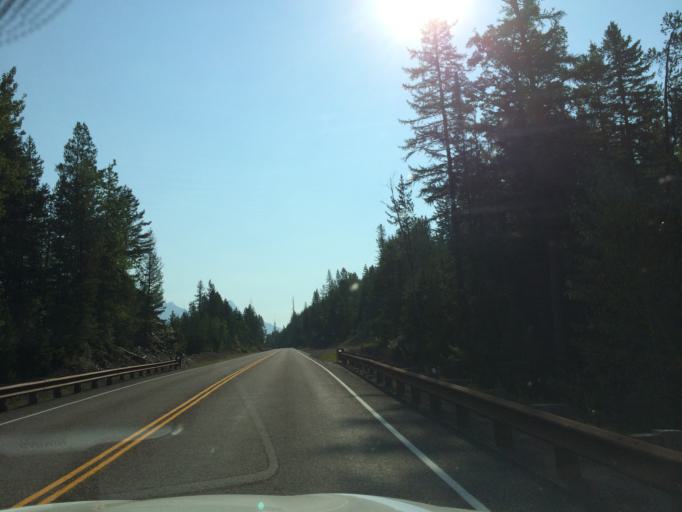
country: US
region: Montana
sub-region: Flathead County
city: Columbia Falls
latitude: 48.4184
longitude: -113.7425
